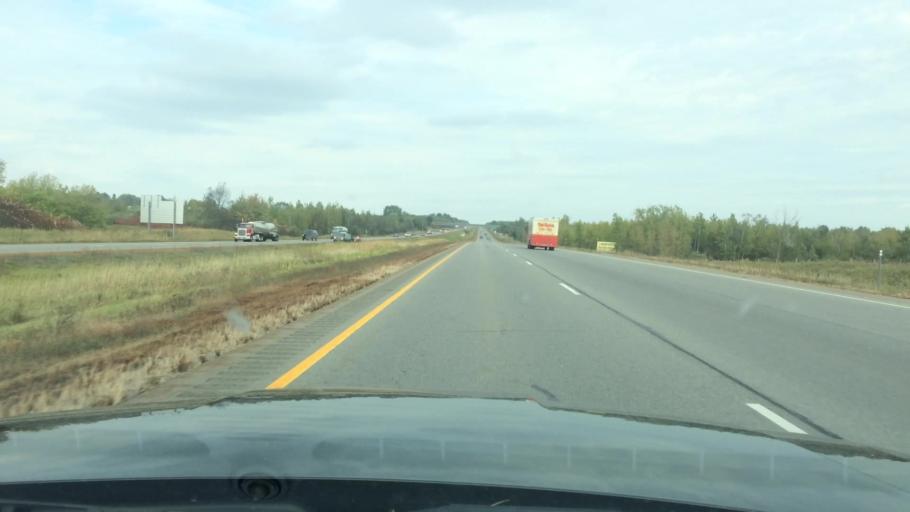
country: US
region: Wisconsin
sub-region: Marathon County
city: Mosinee
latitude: 44.7336
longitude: -89.6796
